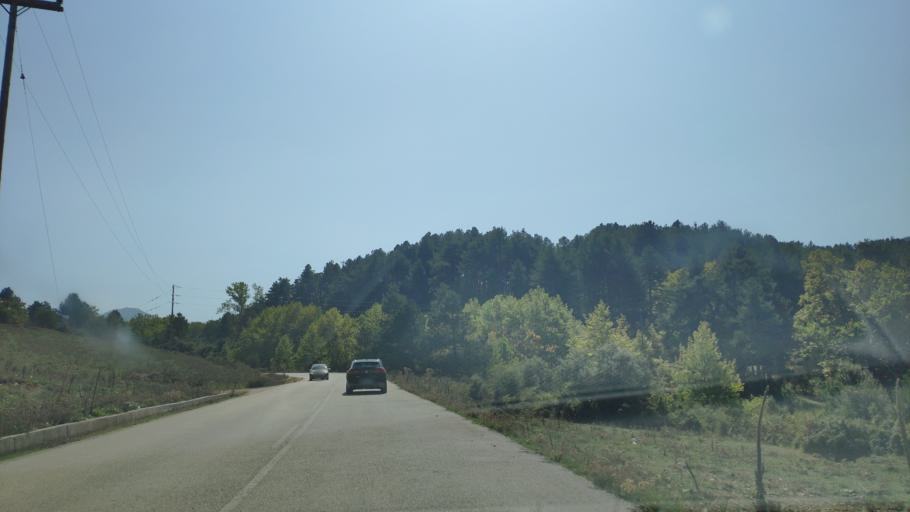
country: GR
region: West Greece
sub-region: Nomos Achaias
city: Kalavryta
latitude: 37.9251
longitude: 22.2928
